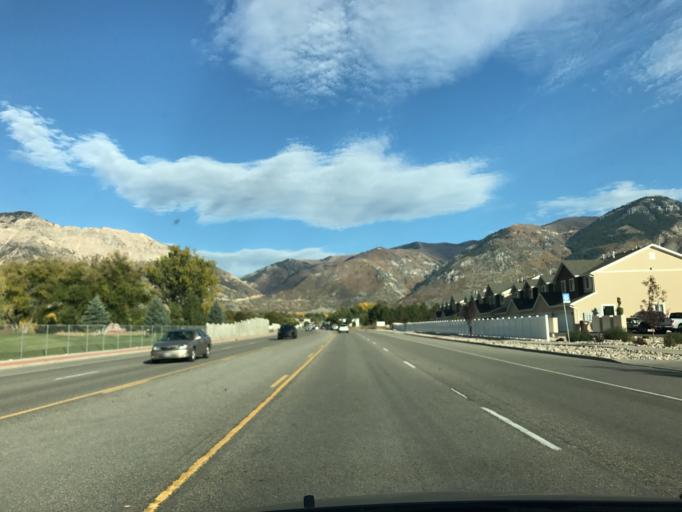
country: US
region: Utah
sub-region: Weber County
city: Pleasant View
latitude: 41.3055
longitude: -111.9822
